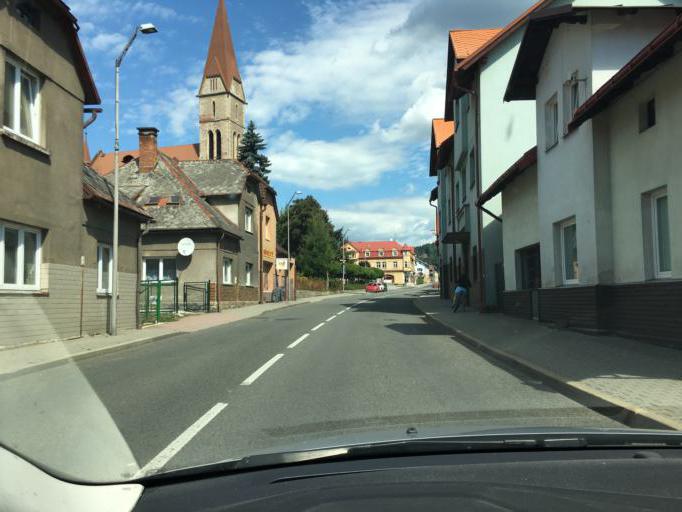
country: CZ
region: Liberecky
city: Velke Hamry
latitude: 50.7163
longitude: 15.3148
